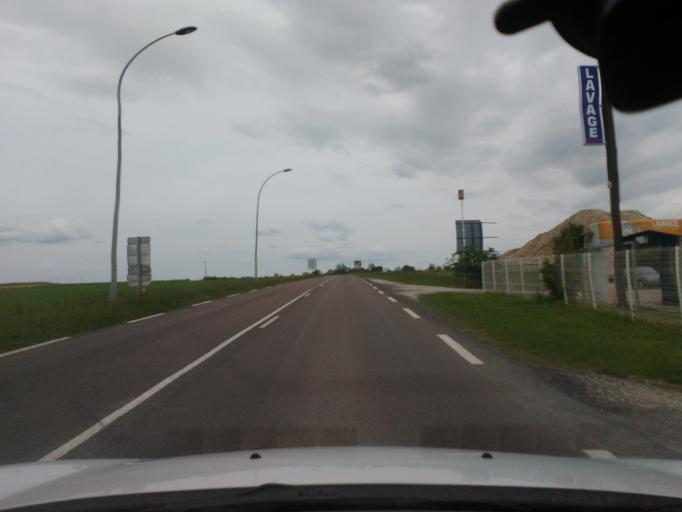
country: FR
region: Champagne-Ardenne
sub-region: Departement de l'Aube
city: Bar-sur-Aube
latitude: 48.2267
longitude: 4.7242
